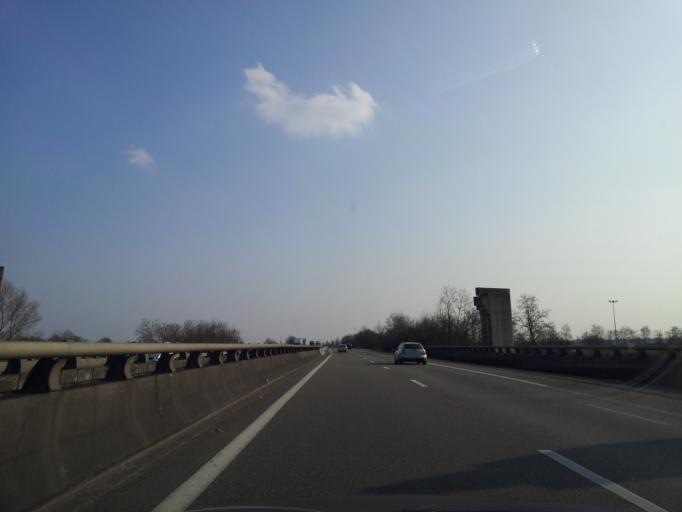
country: FR
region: Alsace
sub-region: Departement du Haut-Rhin
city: Meyenheim
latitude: 47.9150
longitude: 7.3629
